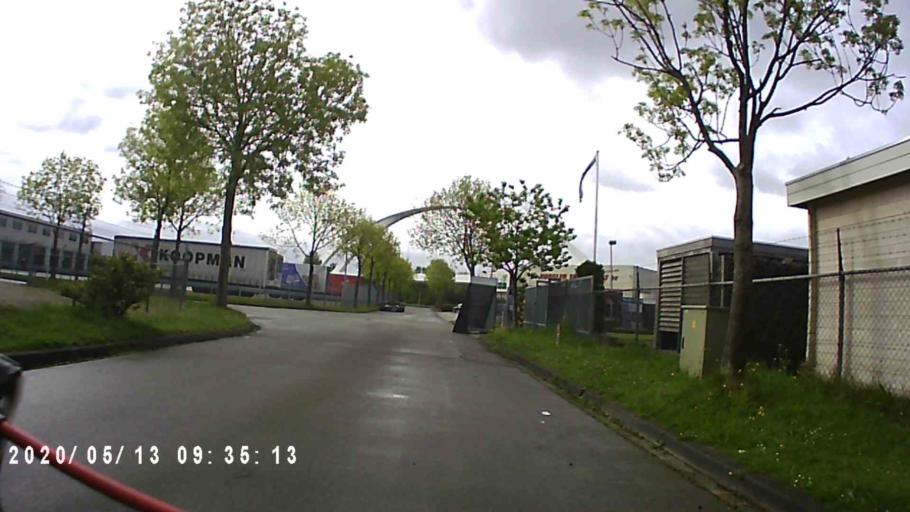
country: NL
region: Groningen
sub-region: Gemeente Zuidhorn
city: Noordhorn
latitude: 53.2548
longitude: 6.3899
